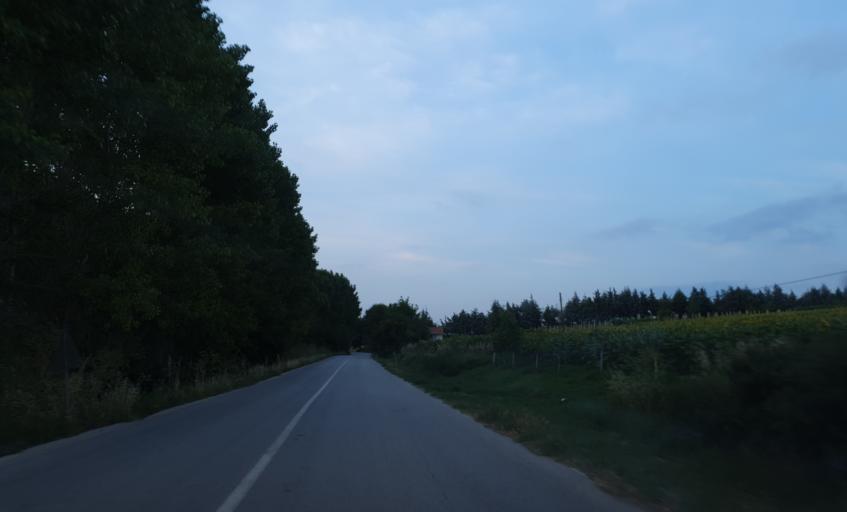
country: TR
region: Tekirdag
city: Beyazkoy
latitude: 41.3741
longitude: 27.6114
